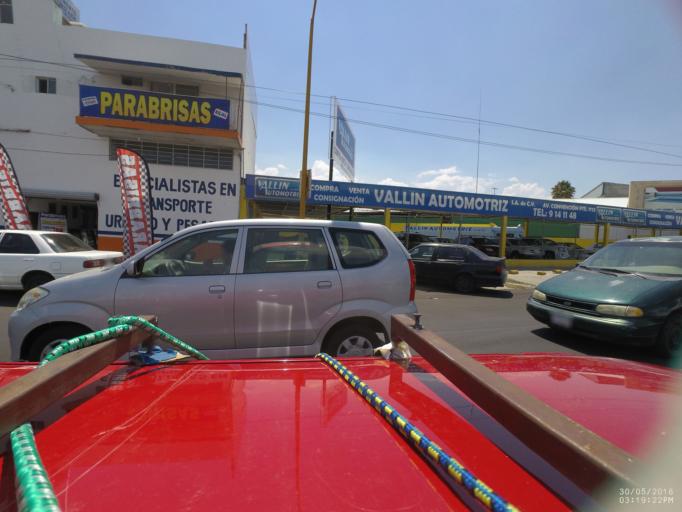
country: MX
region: Aguascalientes
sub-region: Aguascalientes
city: Aguascalientes
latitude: 21.8914
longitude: -102.3126
